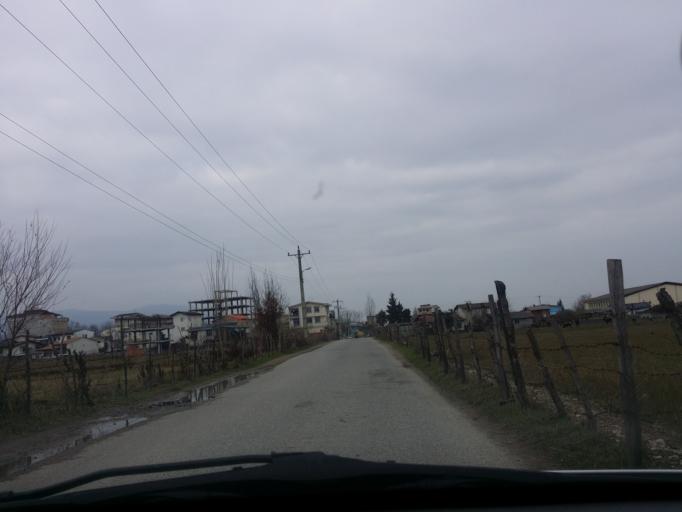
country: IR
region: Mazandaran
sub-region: Nowshahr
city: Nowshahr
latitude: 36.6435
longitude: 51.4834
